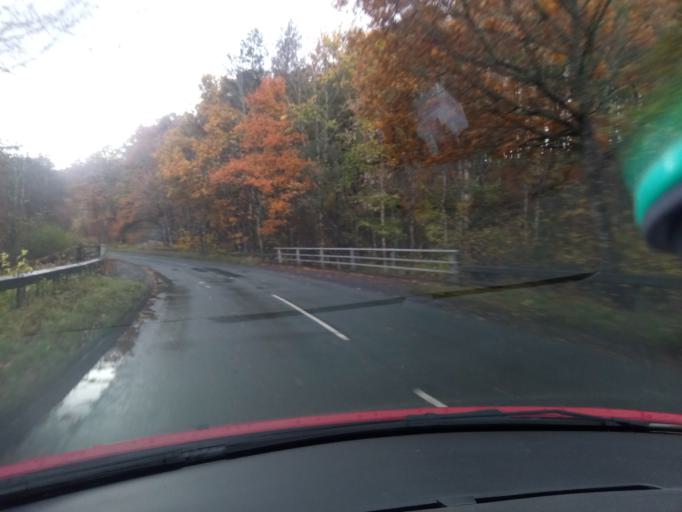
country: GB
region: England
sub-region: Northumberland
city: Birtley
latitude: 55.1047
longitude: -2.2376
